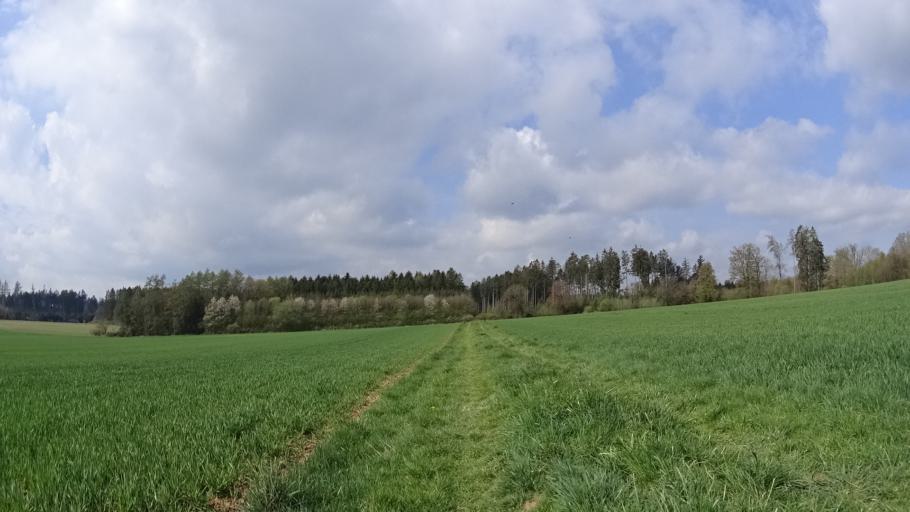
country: DE
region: Bavaria
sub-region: Upper Bavaria
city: Bohmfeld
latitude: 48.8906
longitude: 11.4003
